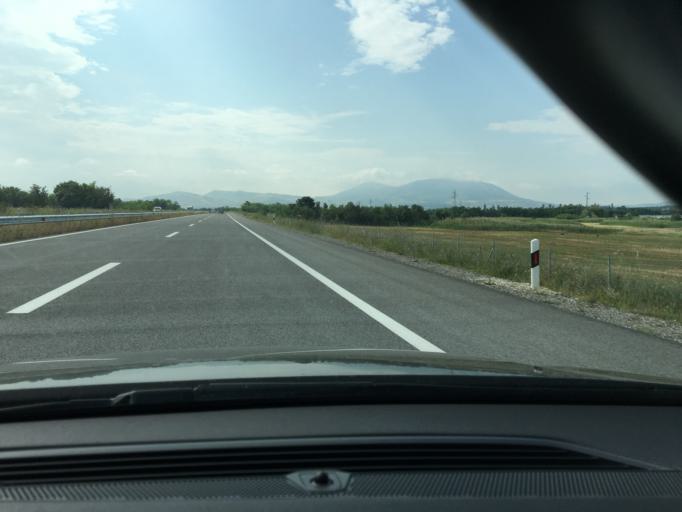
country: MK
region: Sveti Nikole
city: Sveti Nikole
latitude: 41.8392
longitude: 21.9832
